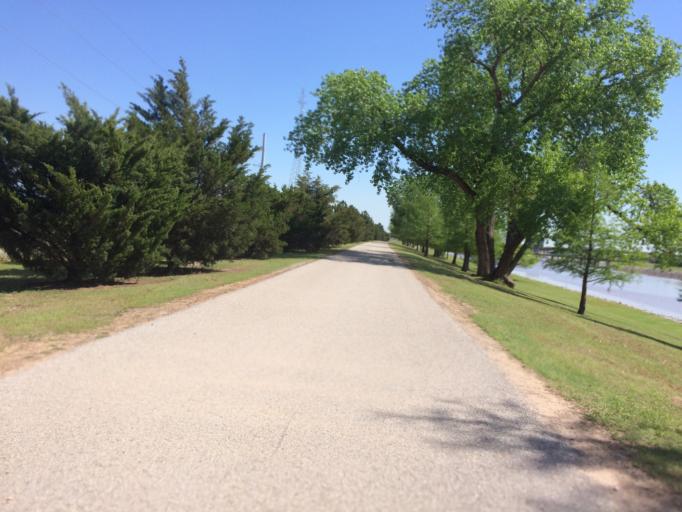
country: US
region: Oklahoma
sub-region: Oklahoma County
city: Oklahoma City
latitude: 35.4528
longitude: -97.5096
